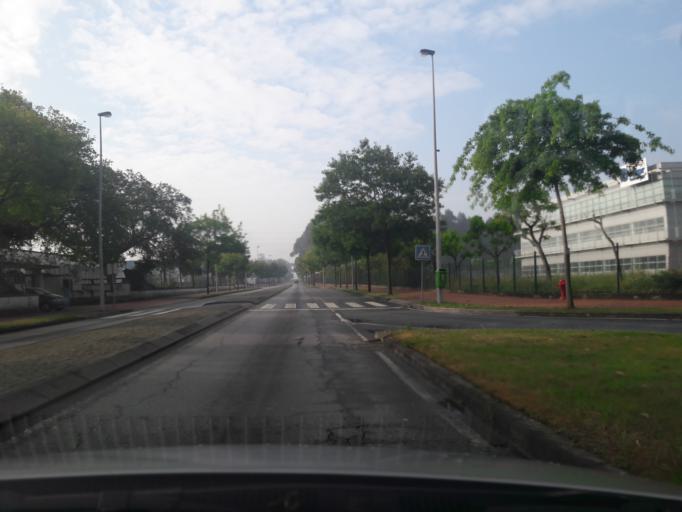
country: PT
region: Porto
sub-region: Vila do Conde
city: Arvore
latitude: 41.3251
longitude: -8.7158
